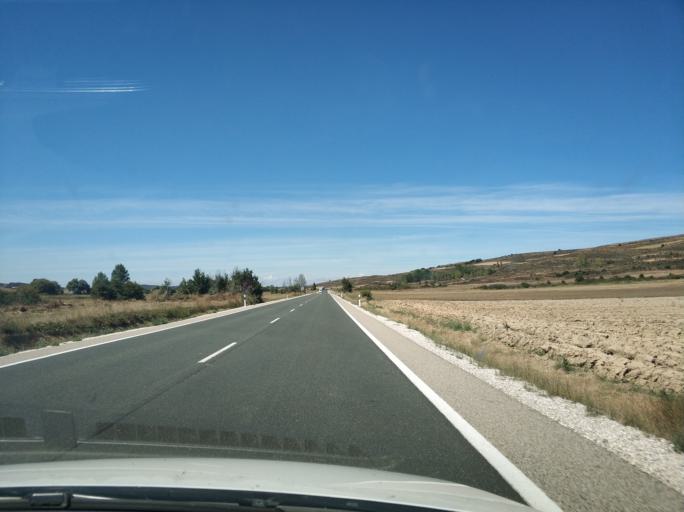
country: ES
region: Castille and Leon
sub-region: Provincia de Burgos
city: Tubilla del Agua
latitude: 42.6483
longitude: -3.8882
